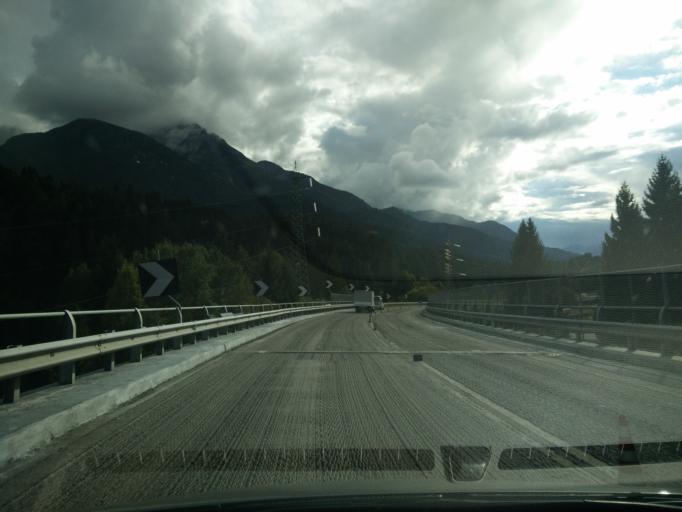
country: IT
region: Veneto
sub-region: Provincia di Belluno
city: Lozzo di Cadore
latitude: 46.4866
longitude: 12.4508
